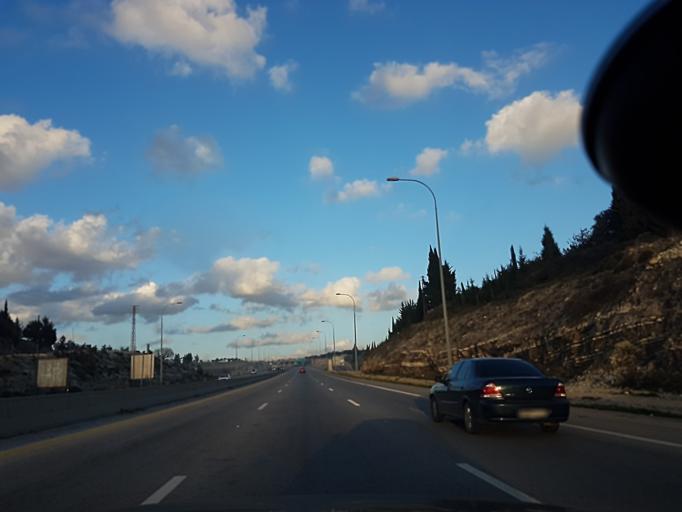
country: LB
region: Liban-Sud
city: Sidon
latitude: 33.4211
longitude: 35.2987
